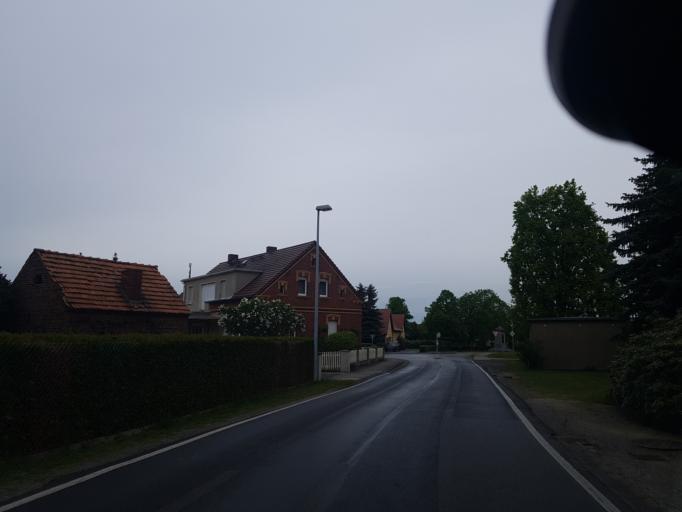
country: DE
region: Brandenburg
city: Spremberg
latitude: 51.6743
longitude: 14.4401
